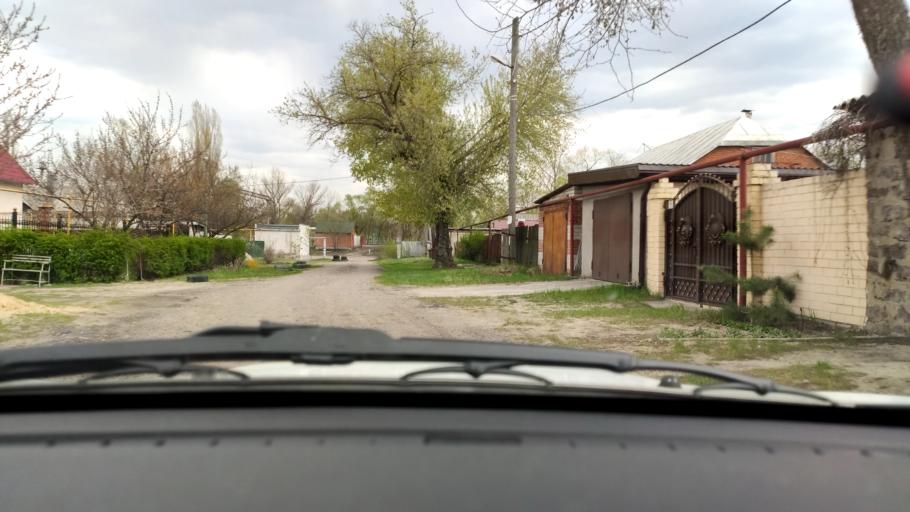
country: RU
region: Voronezj
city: Somovo
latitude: 51.7376
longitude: 39.3467
